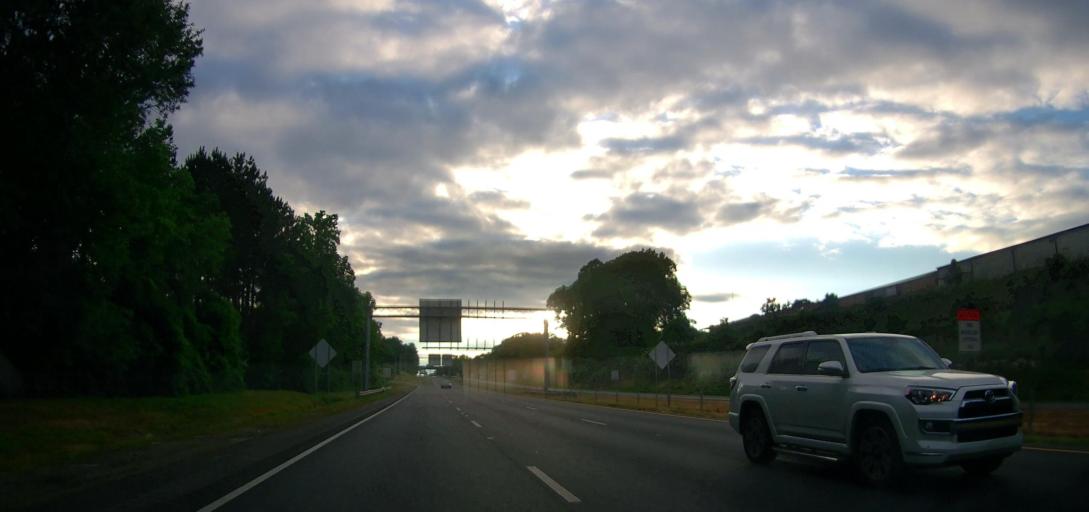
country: US
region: Georgia
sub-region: Clarke County
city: Athens
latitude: 33.9781
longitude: -83.3587
